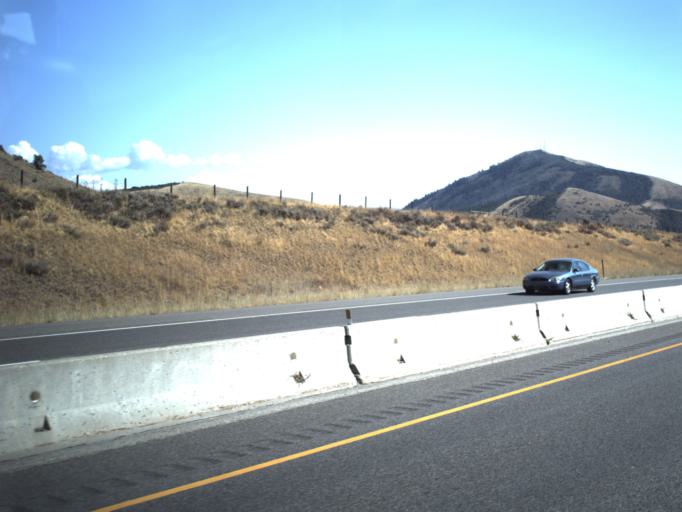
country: US
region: Utah
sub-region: Cache County
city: Wellsville
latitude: 41.5779
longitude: -111.9730
